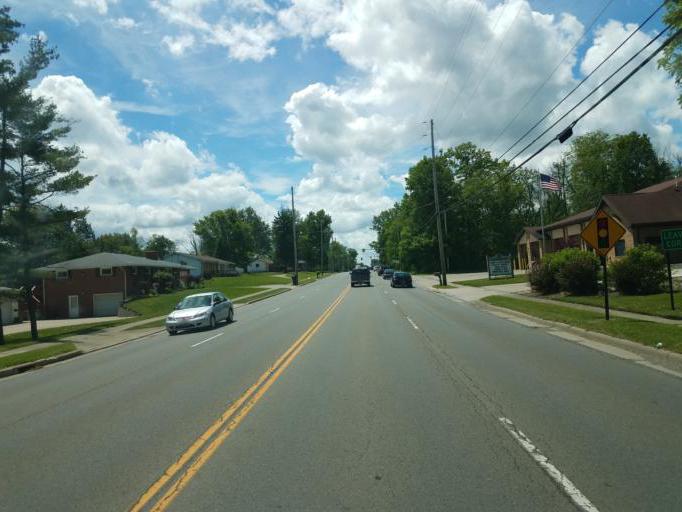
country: US
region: Ohio
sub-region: Richland County
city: Ontario
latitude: 40.7491
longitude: -82.5900
